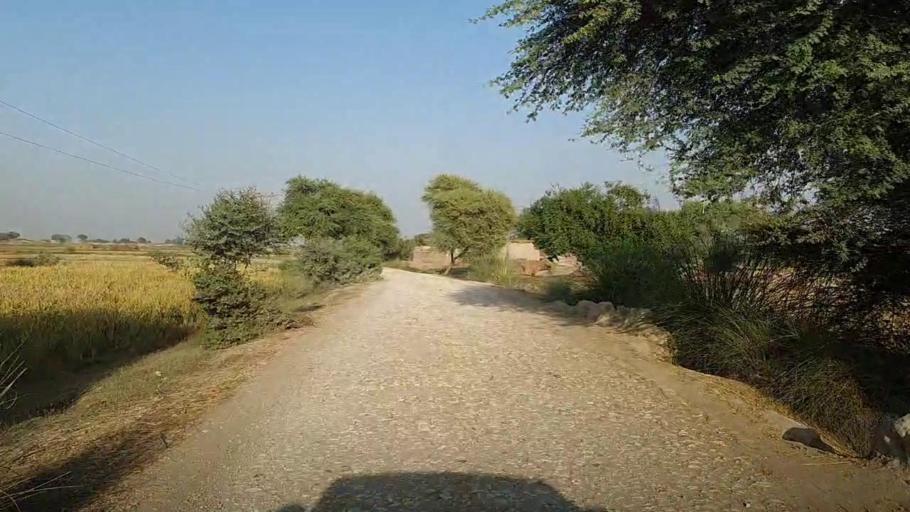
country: PK
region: Sindh
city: Kashmor
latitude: 28.4210
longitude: 69.4197
